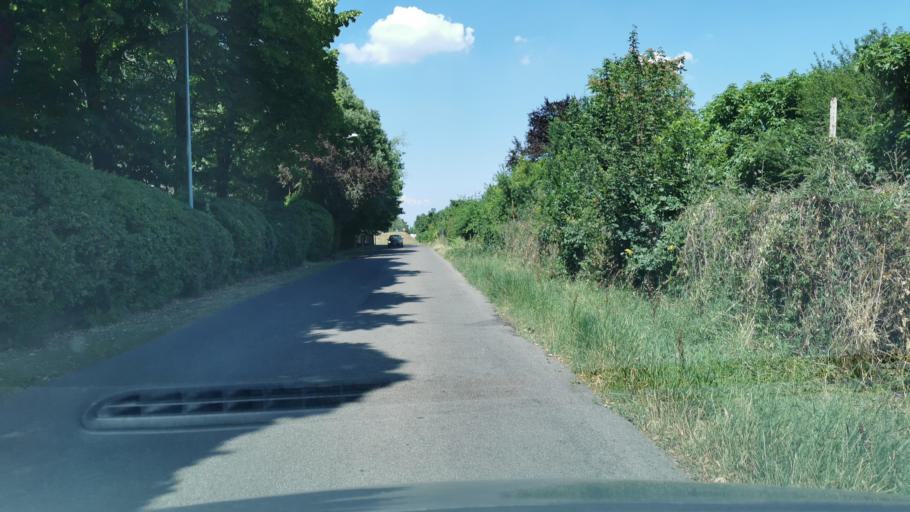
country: IT
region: Emilia-Romagna
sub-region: Provincia di Modena
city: Carpi Centro
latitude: 44.7951
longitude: 10.8888
